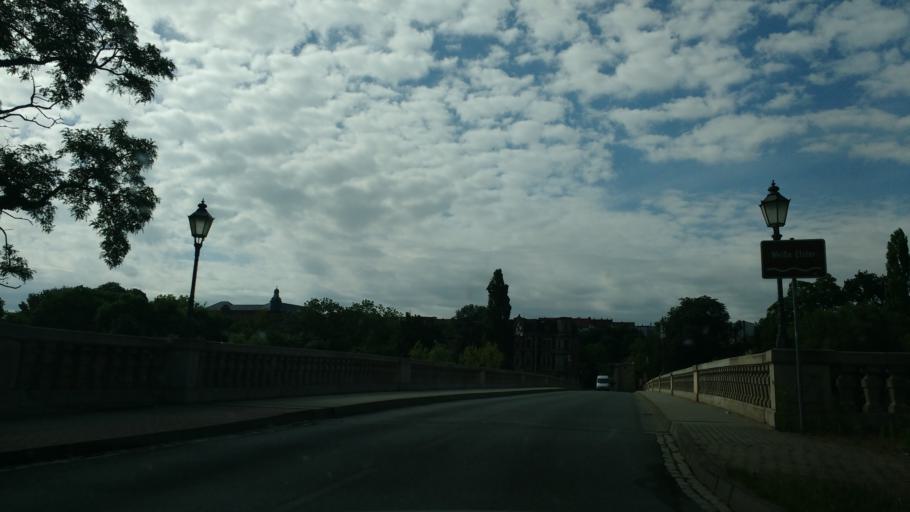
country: DE
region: Saxony-Anhalt
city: Zeitz
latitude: 51.0558
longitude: 12.1368
